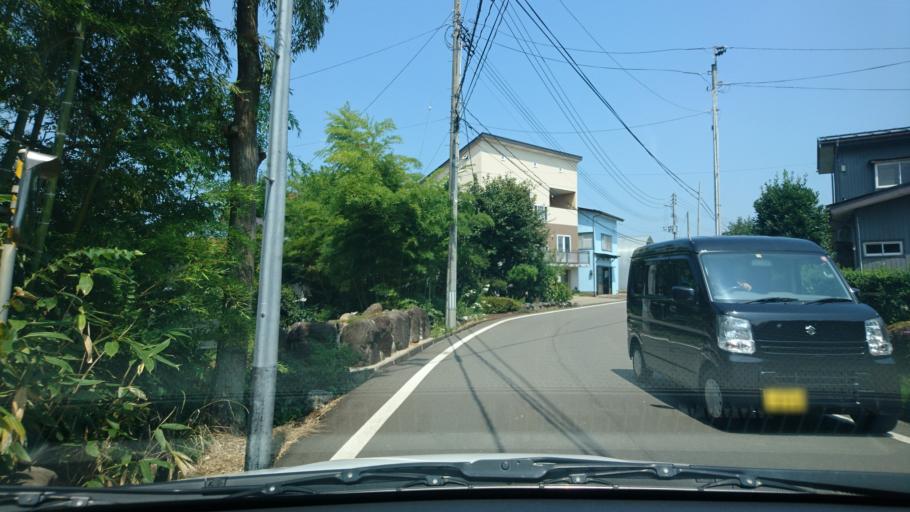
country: JP
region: Niigata
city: Arai
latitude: 37.0701
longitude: 138.2457
